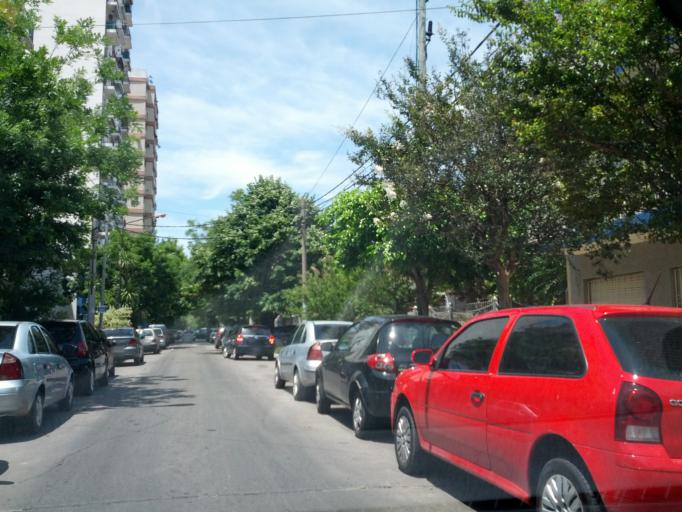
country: AR
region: Buenos Aires
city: San Justo
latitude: -34.6424
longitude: -58.5700
